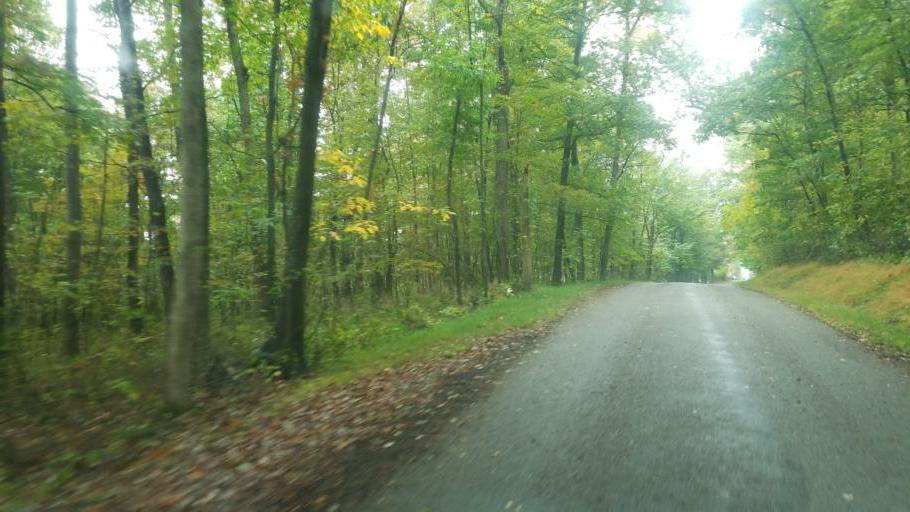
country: US
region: Ohio
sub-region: Ashland County
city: Loudonville
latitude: 40.5617
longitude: -82.2940
